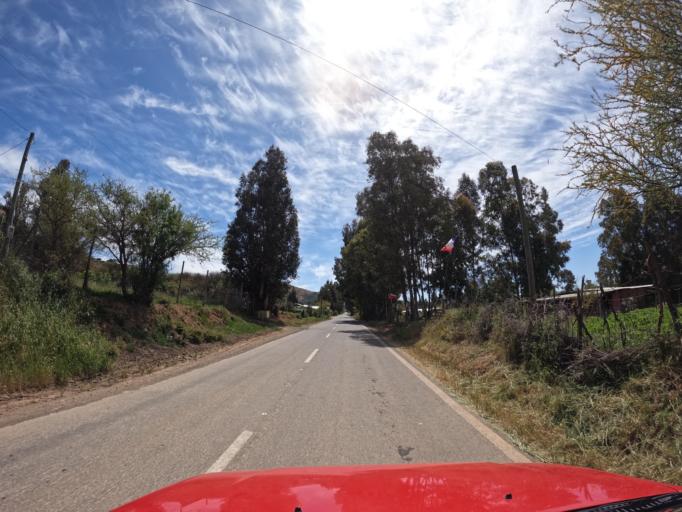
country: CL
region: Maule
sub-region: Provincia de Talca
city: Talca
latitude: -35.0580
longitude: -71.7412
